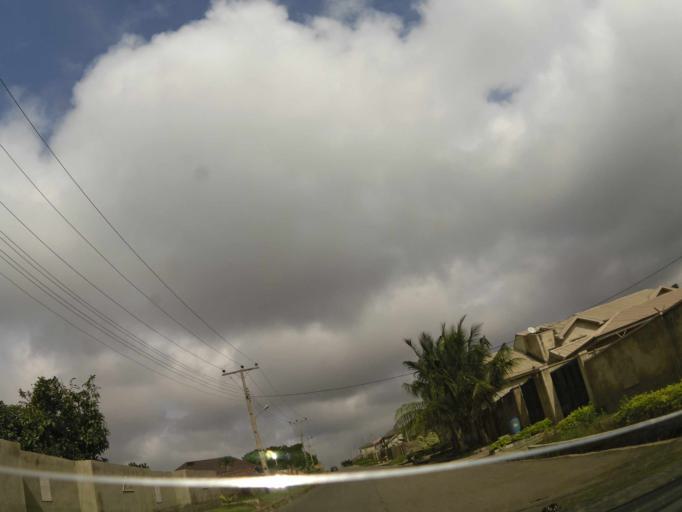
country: NG
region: Oyo
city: Ibadan
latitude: 7.4365
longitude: 3.9584
